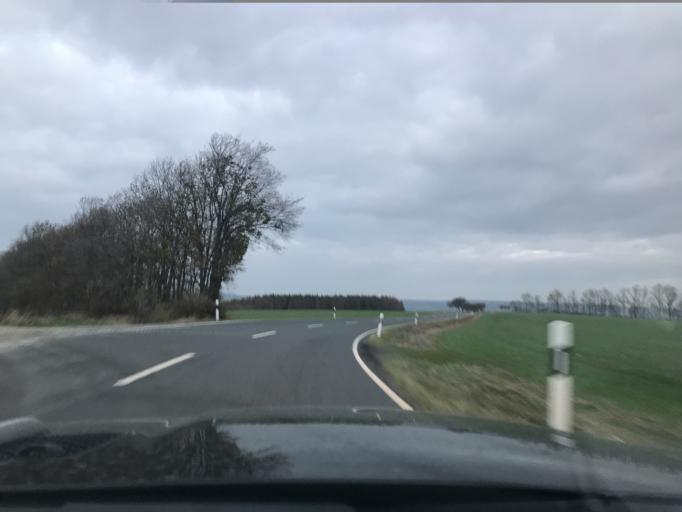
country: DE
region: Thuringia
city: Kullstedt
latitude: 51.2904
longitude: 10.2940
